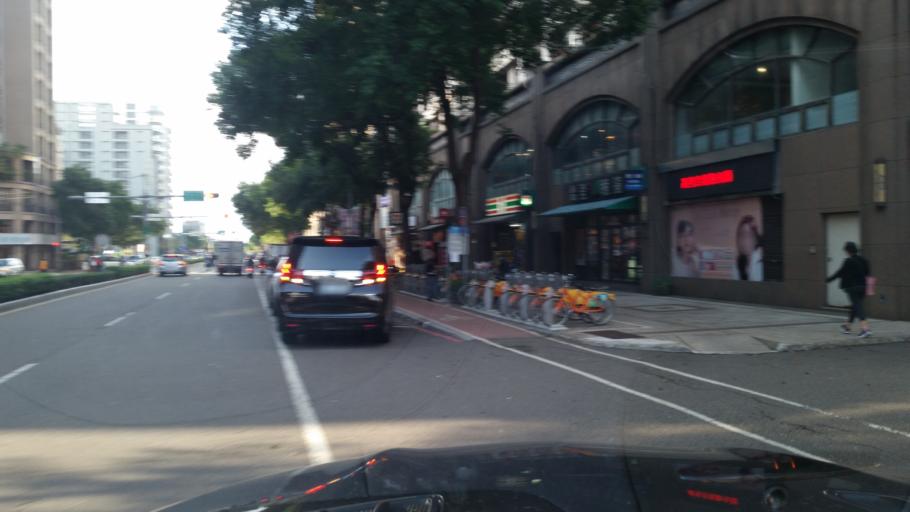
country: TW
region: Taiwan
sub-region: Taoyuan
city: Taoyuan
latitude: 25.0772
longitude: 121.3743
